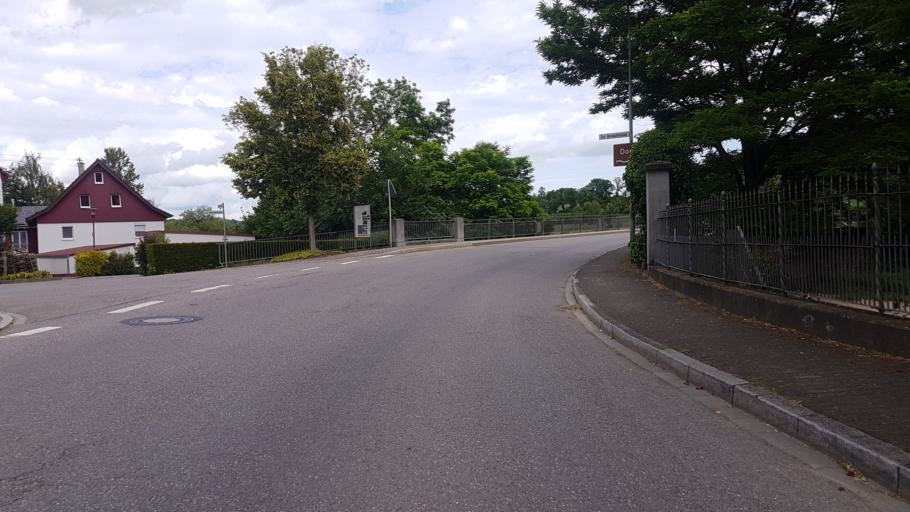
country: DE
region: Baden-Wuerttemberg
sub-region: Tuebingen Region
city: Emeringen
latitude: 48.2147
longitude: 9.5175
